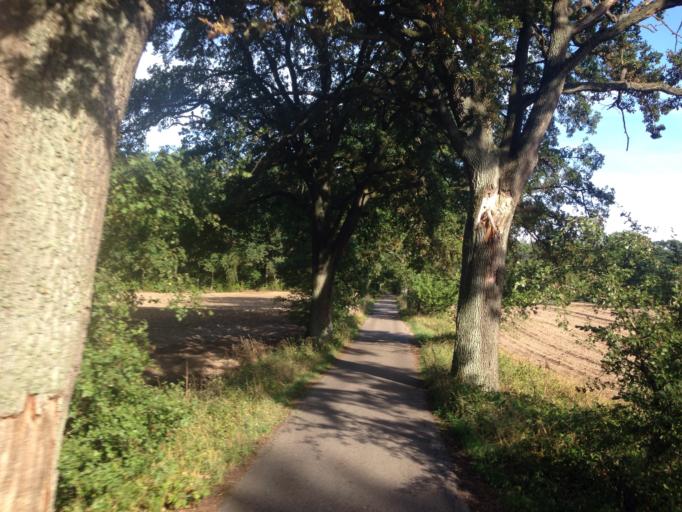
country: PL
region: Warmian-Masurian Voivodeship
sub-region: Powiat dzialdowski
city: Lidzbark
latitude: 53.2475
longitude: 19.7604
